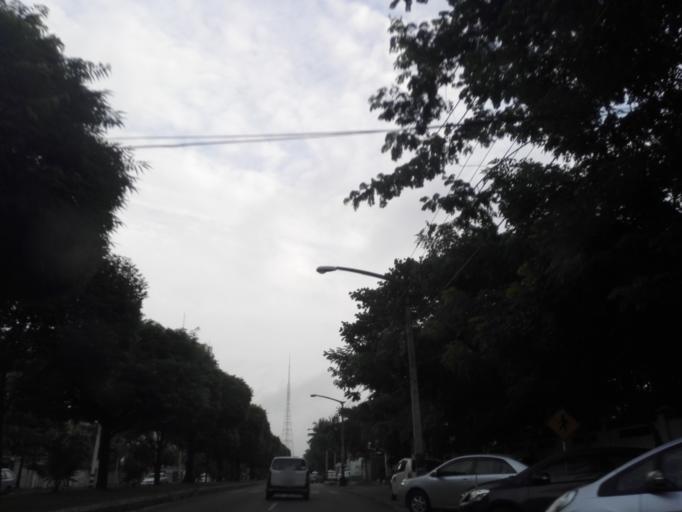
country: MM
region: Yangon
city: Yangon
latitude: 16.8088
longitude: 96.1389
